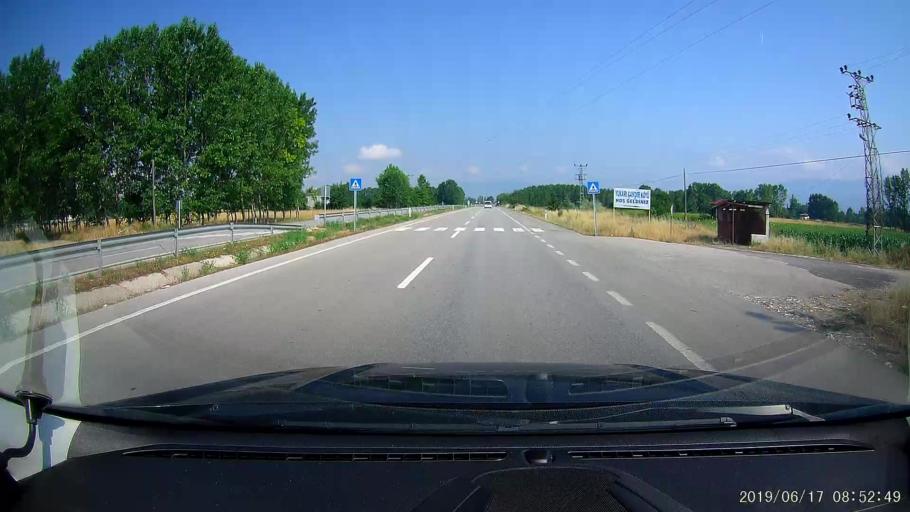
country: TR
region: Tokat
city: Erbaa
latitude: 40.7026
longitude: 36.4908
